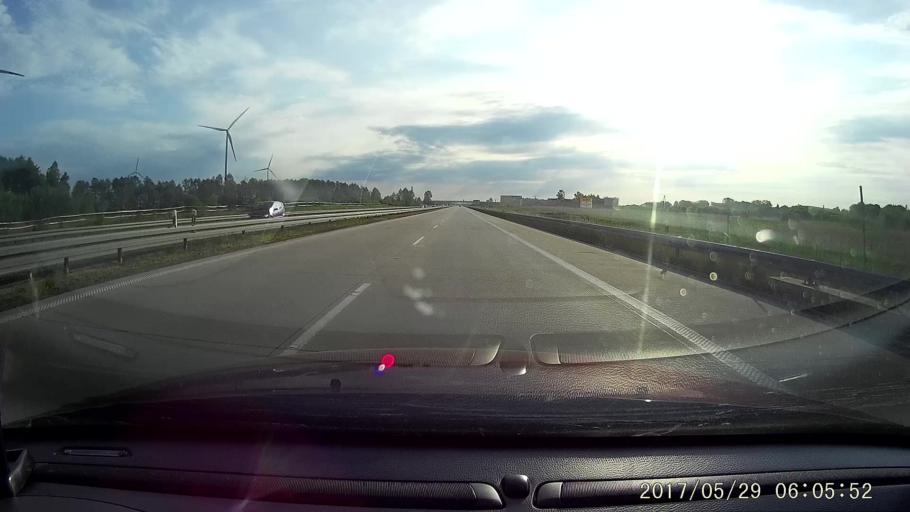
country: PL
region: Lower Silesian Voivodeship
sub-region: Powiat zgorzelecki
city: Lagow
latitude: 51.1763
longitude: 15.0832
